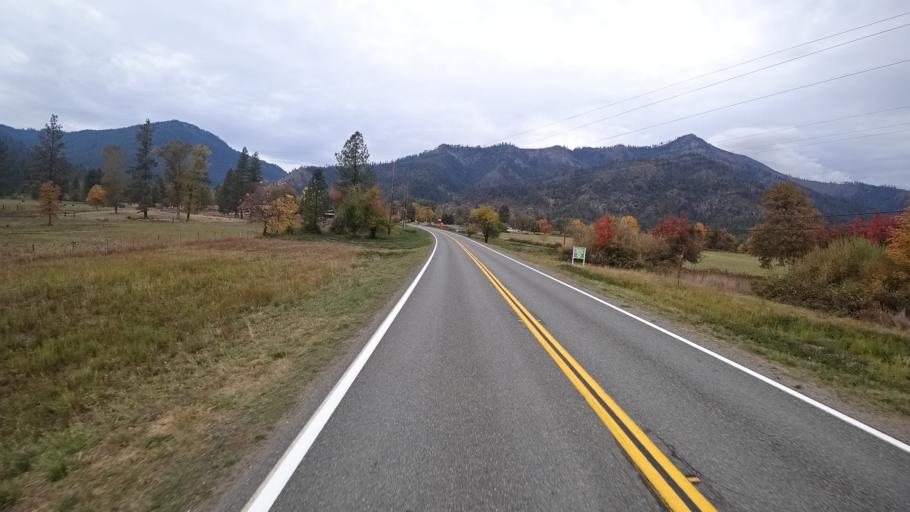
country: US
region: California
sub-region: Siskiyou County
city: Happy Camp
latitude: 41.8391
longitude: -123.1894
